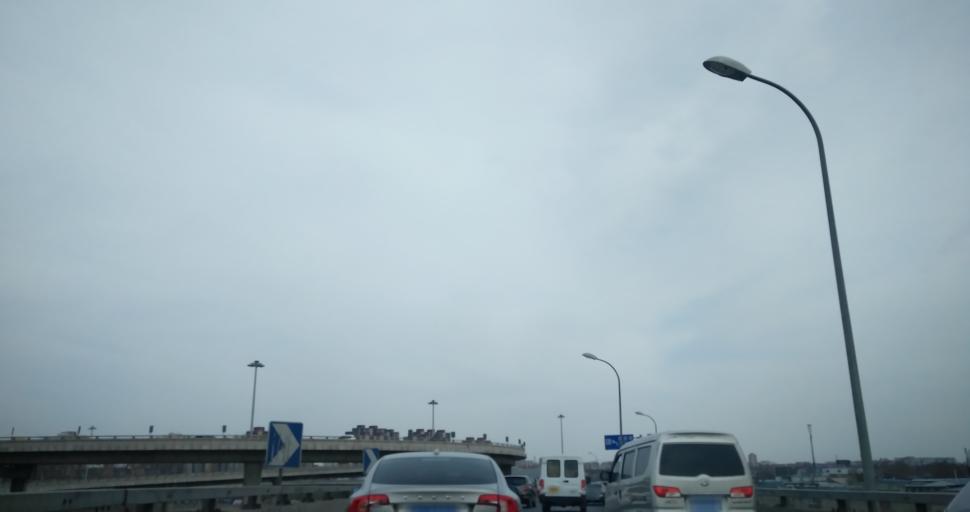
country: CN
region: Beijing
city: Dahongmen
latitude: 39.8314
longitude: 116.4181
